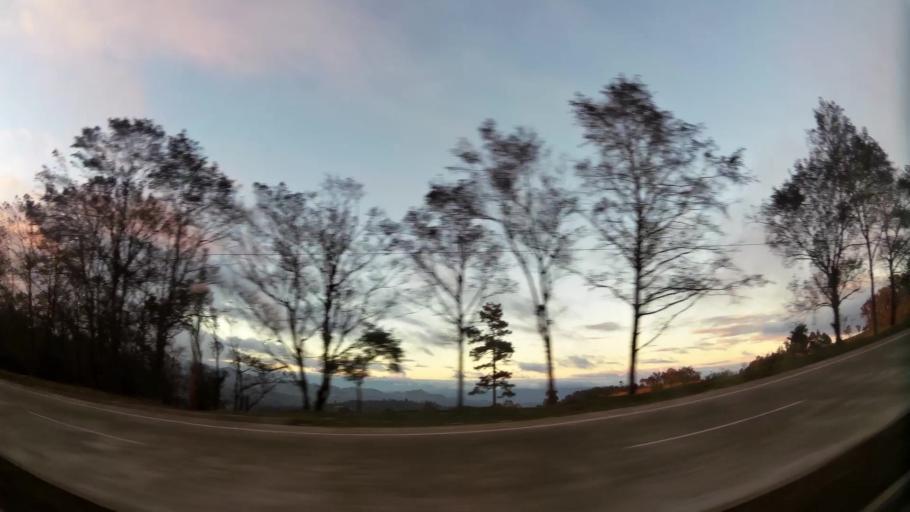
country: GT
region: Solola
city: Concepcion
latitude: 14.8362
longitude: -91.1075
